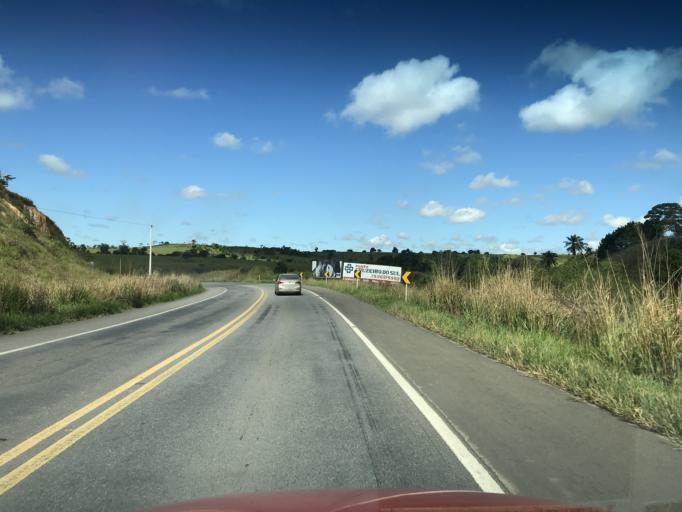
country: BR
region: Bahia
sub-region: Conceicao Do Almeida
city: Muritiba
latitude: -12.9309
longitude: -39.2535
